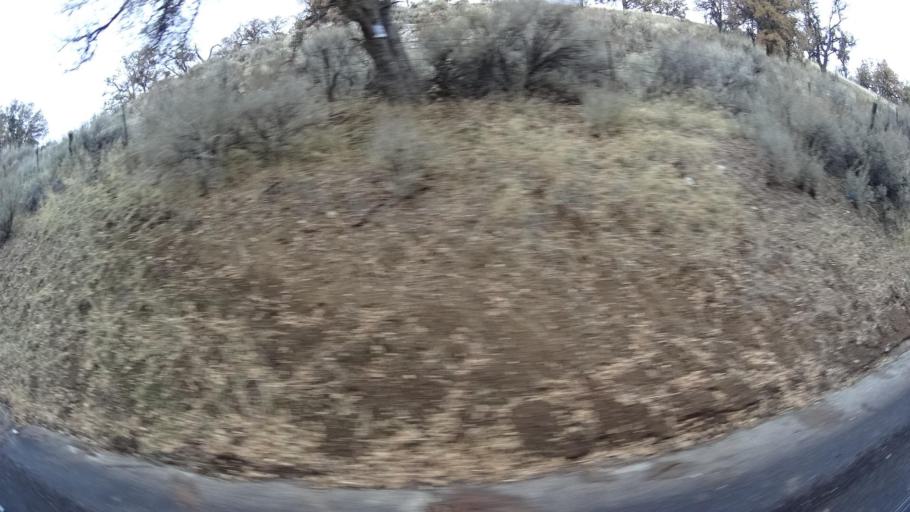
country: US
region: California
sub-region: Kern County
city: Golden Hills
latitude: 35.0961
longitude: -118.5414
